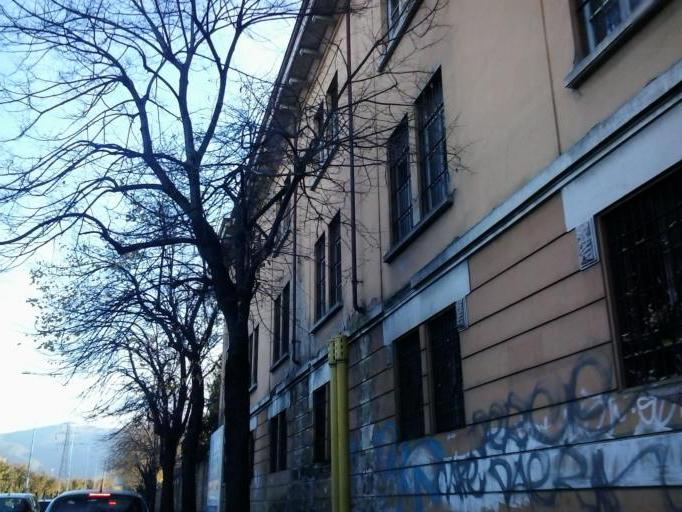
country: IT
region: Lombardy
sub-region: Provincia di Brescia
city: Brescia
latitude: 45.5561
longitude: 10.2024
